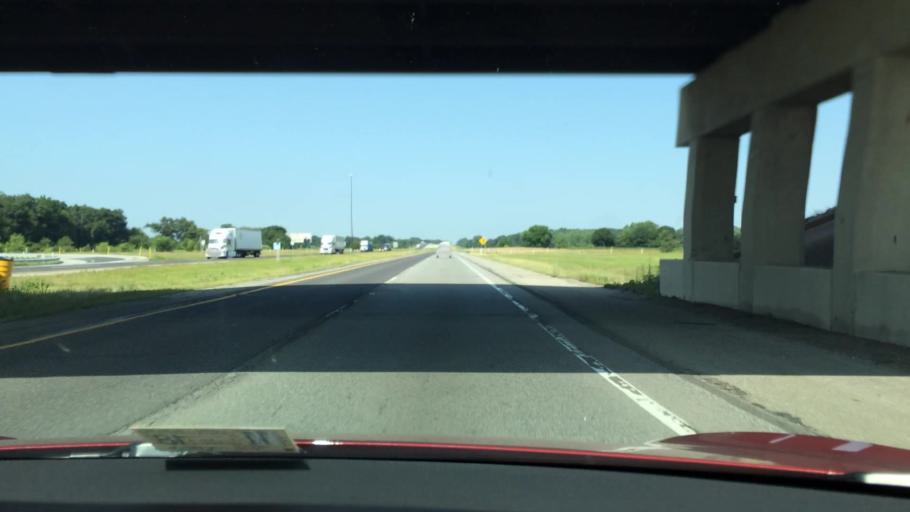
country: US
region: Michigan
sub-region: Saint Joseph County
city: Sturgis
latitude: 41.7539
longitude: -85.4330
